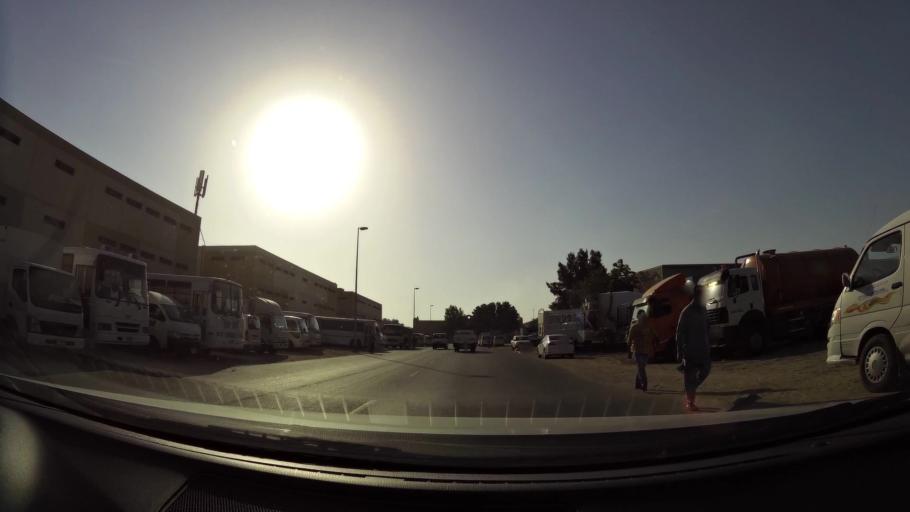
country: AE
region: Dubai
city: Dubai
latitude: 25.1331
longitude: 55.2495
